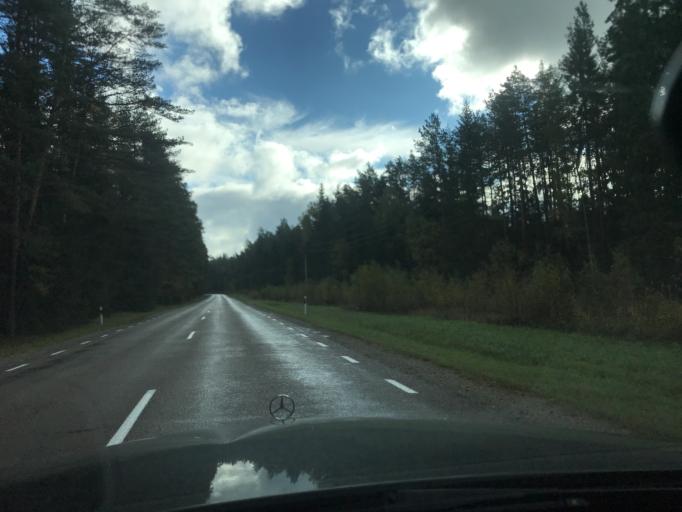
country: EE
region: Valgamaa
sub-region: Torva linn
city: Torva
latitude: 58.0113
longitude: 26.1223
